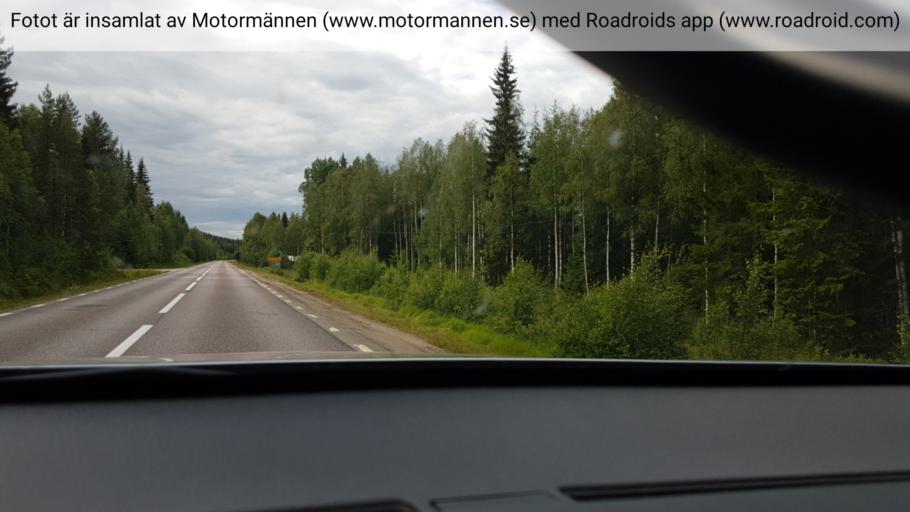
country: NO
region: Hedmark
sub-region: Trysil
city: Innbygda
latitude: 60.9017
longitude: 12.5721
